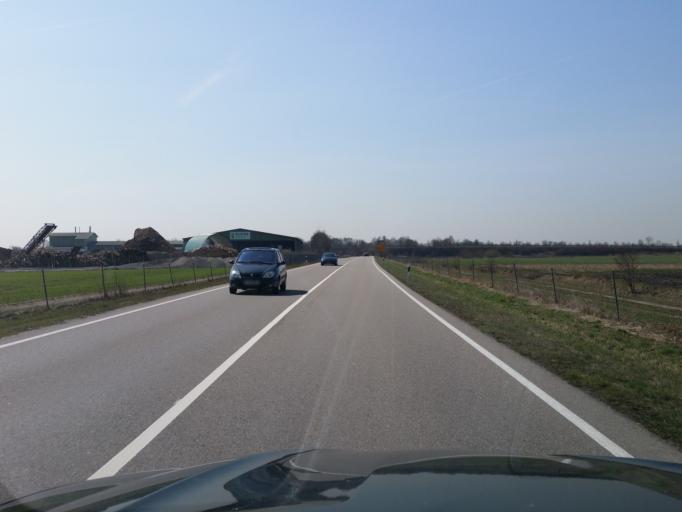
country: DE
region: Bavaria
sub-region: Upper Bavaria
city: Eitting
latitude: 48.3764
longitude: 11.8581
